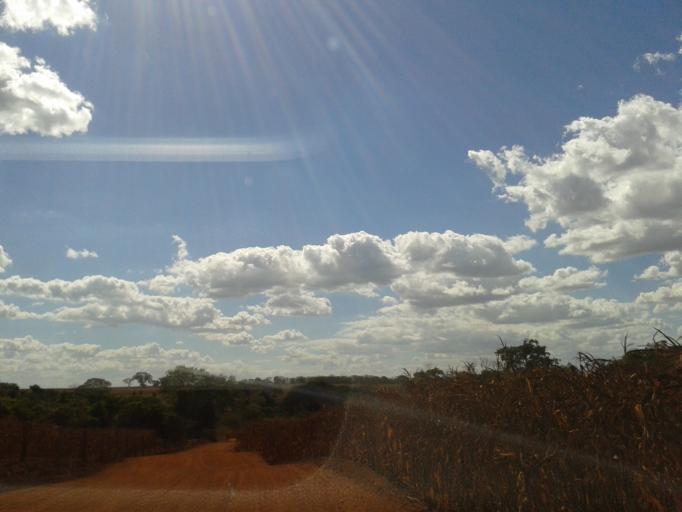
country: BR
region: Minas Gerais
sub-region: Capinopolis
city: Capinopolis
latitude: -18.6140
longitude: -49.4948
